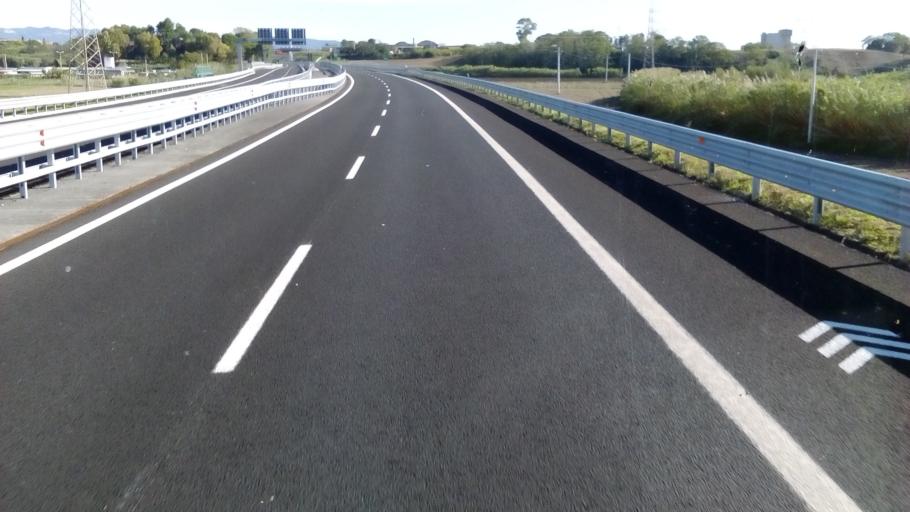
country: IT
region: Latium
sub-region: Provincia di Viterbo
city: Tarquinia
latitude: 42.2525
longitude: 11.7314
